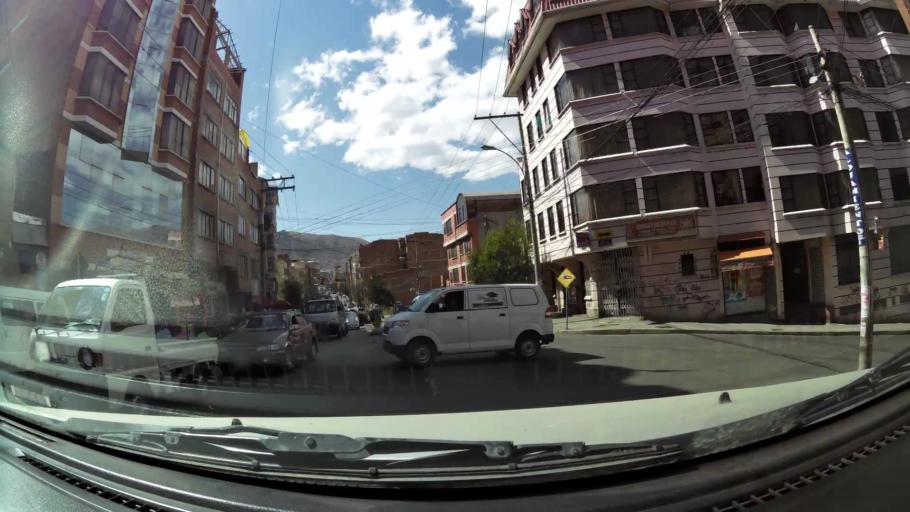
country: BO
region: La Paz
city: La Paz
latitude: -16.4889
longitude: -68.1253
